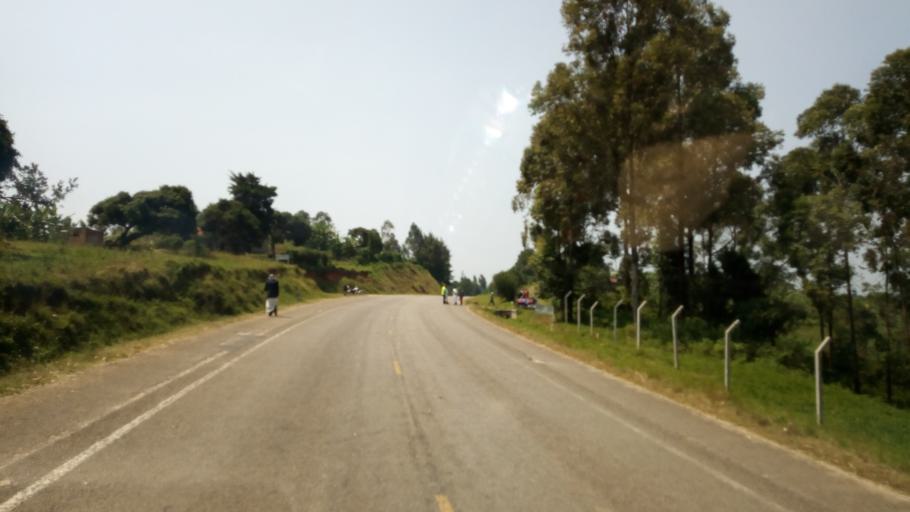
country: UG
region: Western Region
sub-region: Ntungamo District
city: Ntungamo
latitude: -0.8174
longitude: 30.1547
